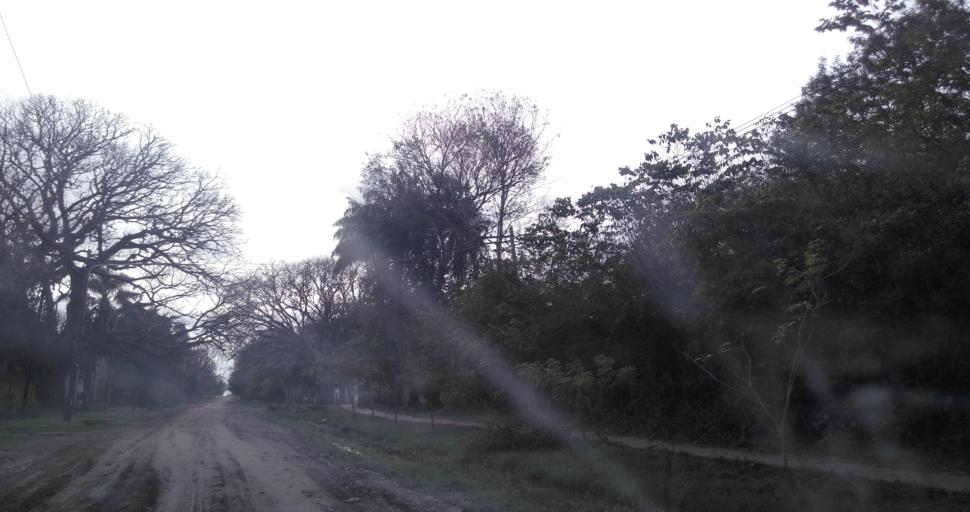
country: AR
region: Chaco
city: Colonia Benitez
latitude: -27.3318
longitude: -58.9528
